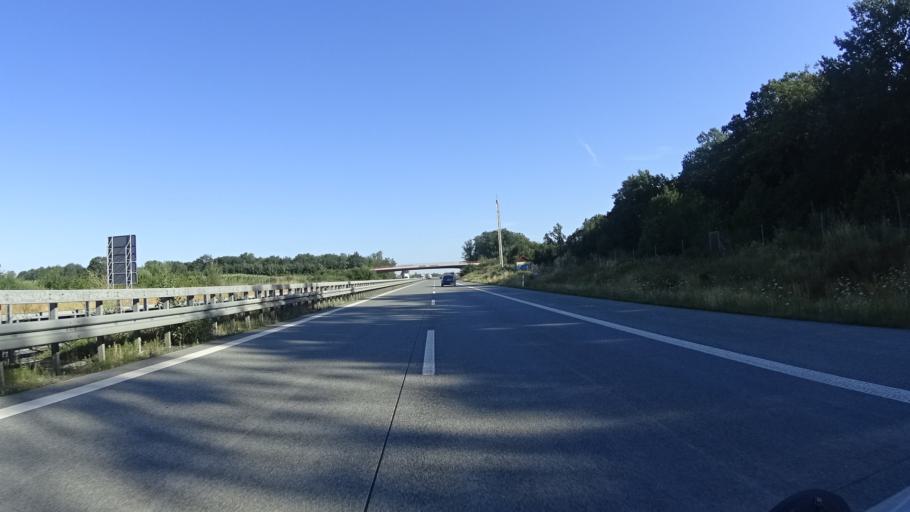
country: DE
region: Saxony
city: Schonfeld
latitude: 51.3189
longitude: 13.7221
